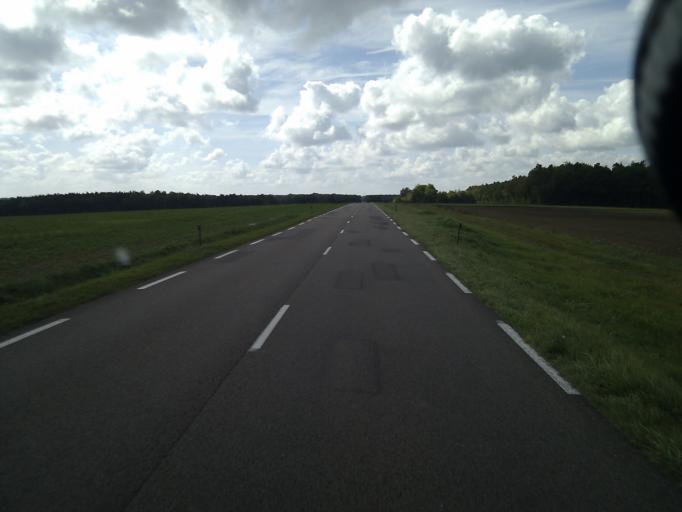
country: FR
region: Bourgogne
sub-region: Departement de la Cote-d'Or
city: Montbard
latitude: 47.6957
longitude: 4.4214
